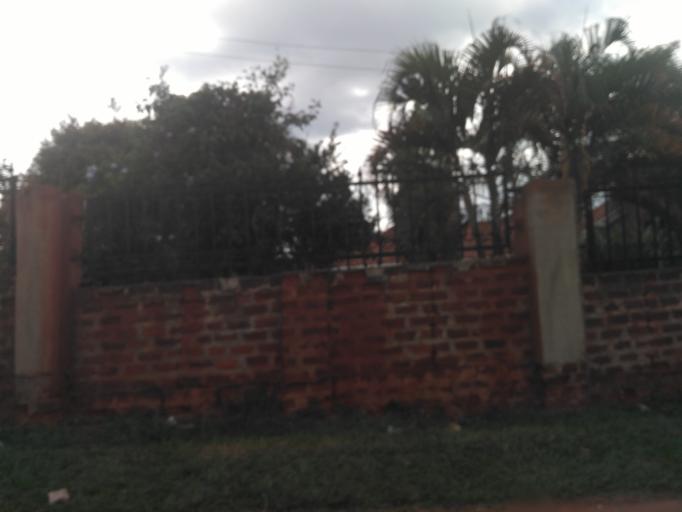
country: UG
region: Eastern Region
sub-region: Jinja District
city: Jinja
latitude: 0.4401
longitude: 33.2002
